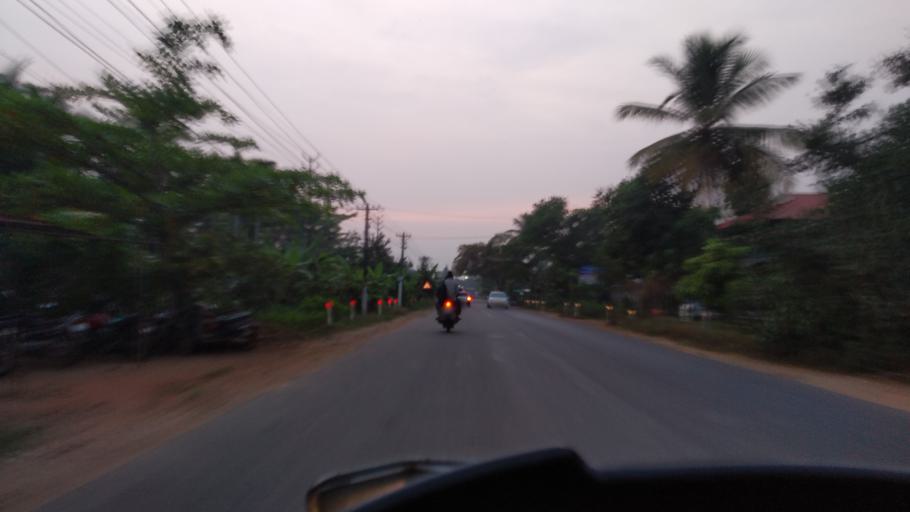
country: IN
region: Kerala
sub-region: Kottayam
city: Kottayam
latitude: 9.5921
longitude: 76.4448
